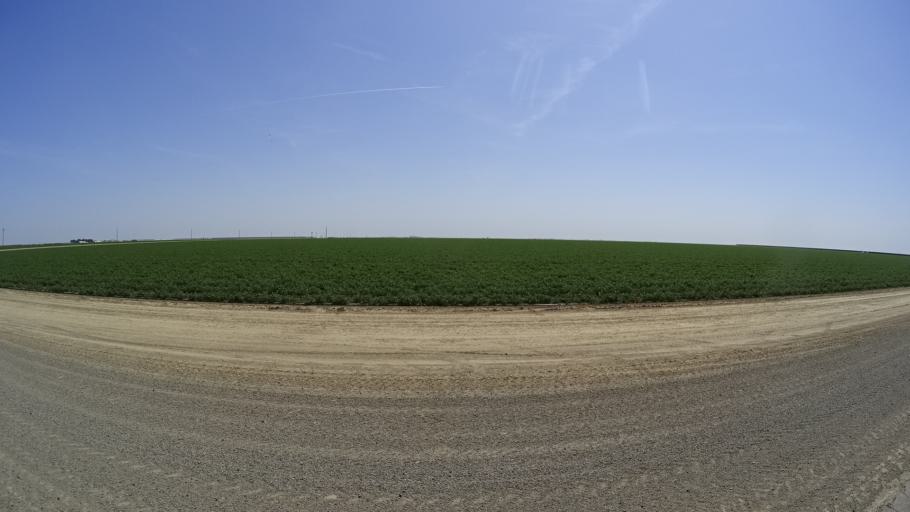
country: US
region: California
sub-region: Kings County
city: Kettleman City
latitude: 36.1214
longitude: -120.0037
